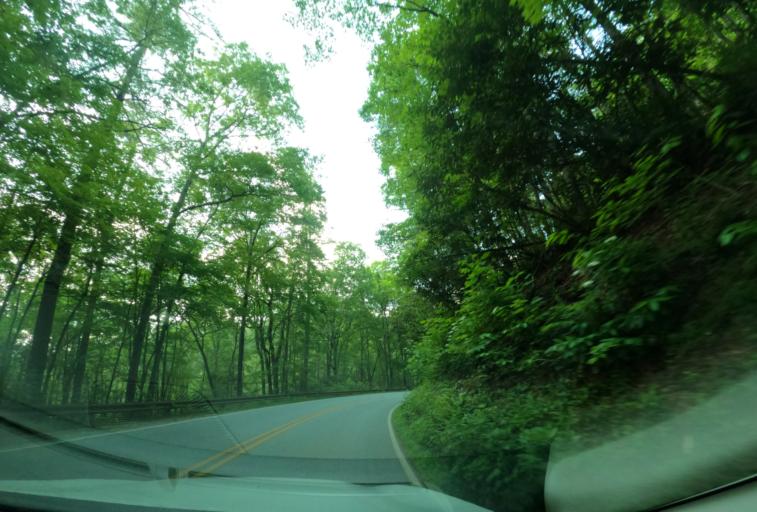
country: US
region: North Carolina
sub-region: Transylvania County
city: Brevard
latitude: 35.1900
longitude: -82.8483
